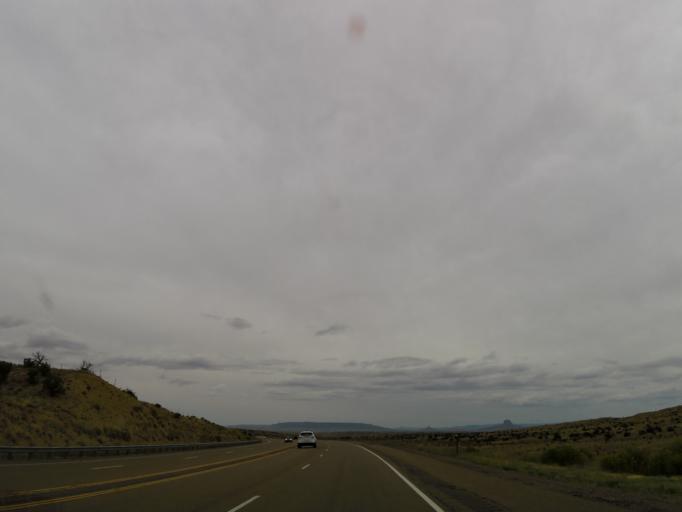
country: US
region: New Mexico
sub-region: Sandoval County
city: Jemez Pueblo
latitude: 35.7503
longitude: -106.9400
